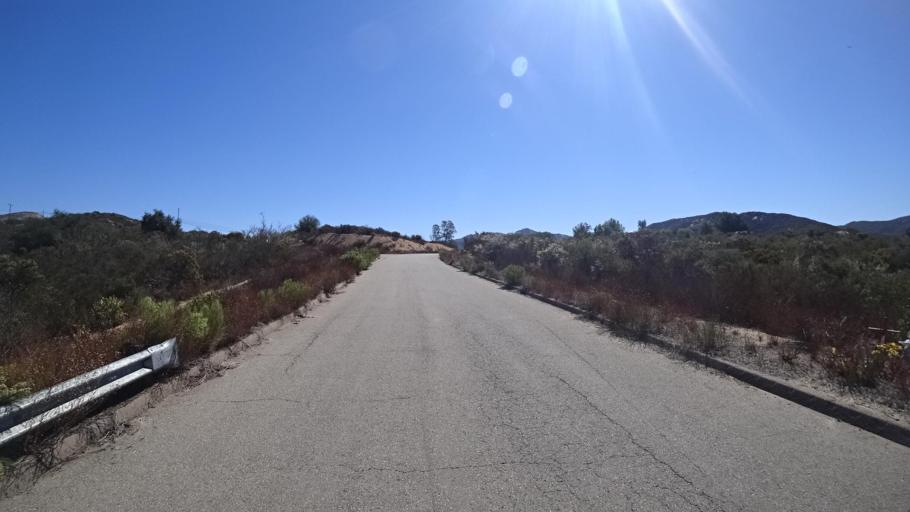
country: US
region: California
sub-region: San Diego County
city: Alpine
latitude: 32.7596
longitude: -116.7723
